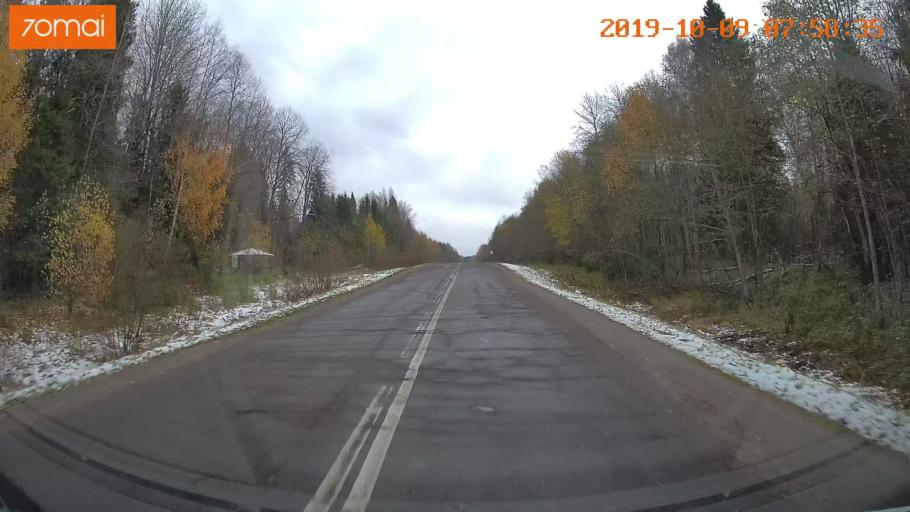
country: RU
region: Jaroslavl
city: Kukoboy
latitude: 58.6970
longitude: 39.9684
